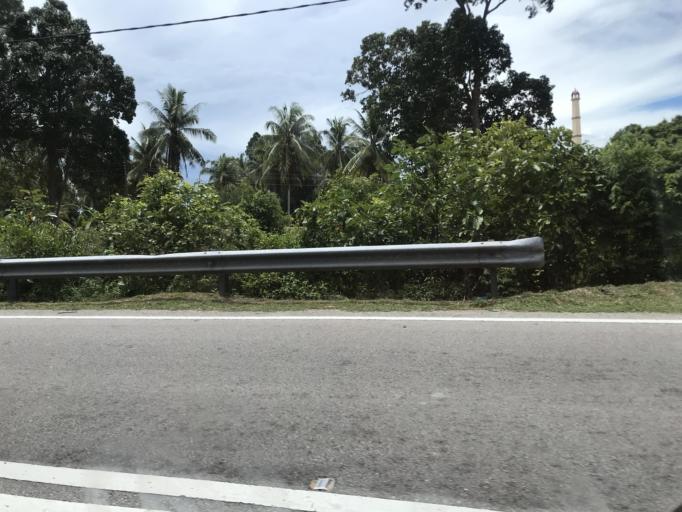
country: MY
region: Kelantan
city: Tumpat
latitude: 6.1749
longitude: 102.1999
